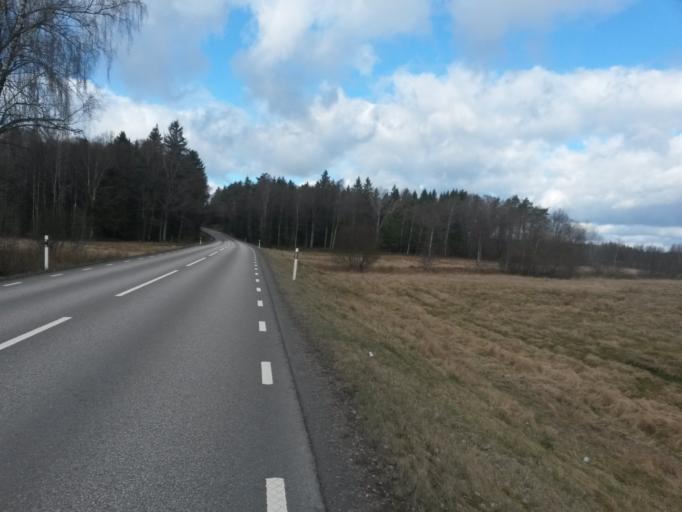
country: SE
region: Vaestra Goetaland
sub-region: Vargarda Kommun
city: Vargarda
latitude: 58.0581
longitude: 12.7545
